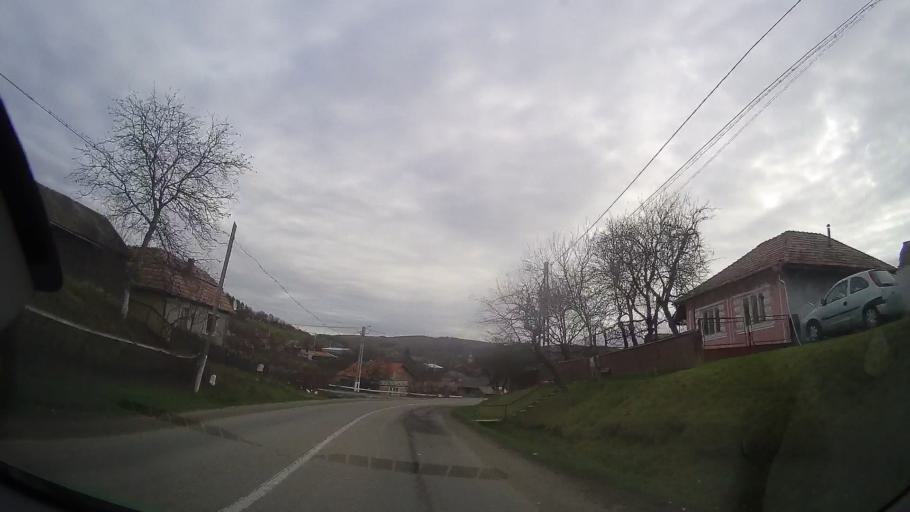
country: RO
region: Bistrita-Nasaud
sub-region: Comuna Budesti
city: Budesti
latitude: 46.8784
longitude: 24.2411
